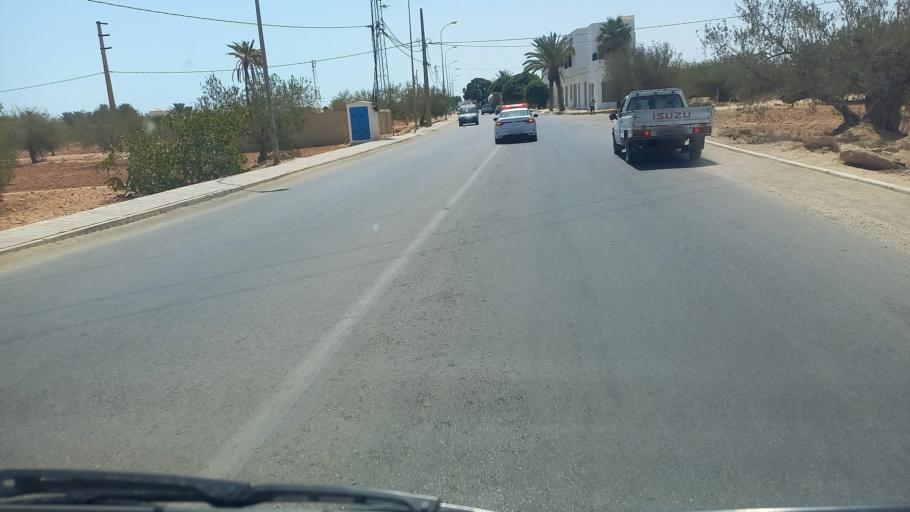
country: TN
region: Madanin
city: Houmt Souk
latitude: 33.7783
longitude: 10.8924
